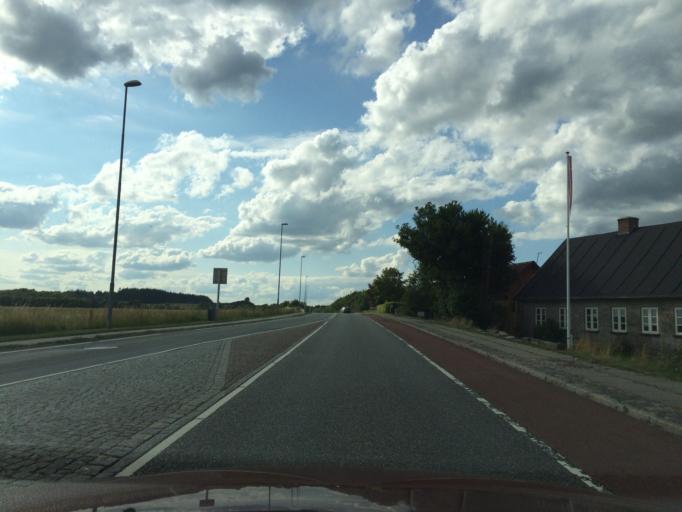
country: DK
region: Central Jutland
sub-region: Arhus Kommune
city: Sabro
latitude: 56.2233
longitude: 9.9689
